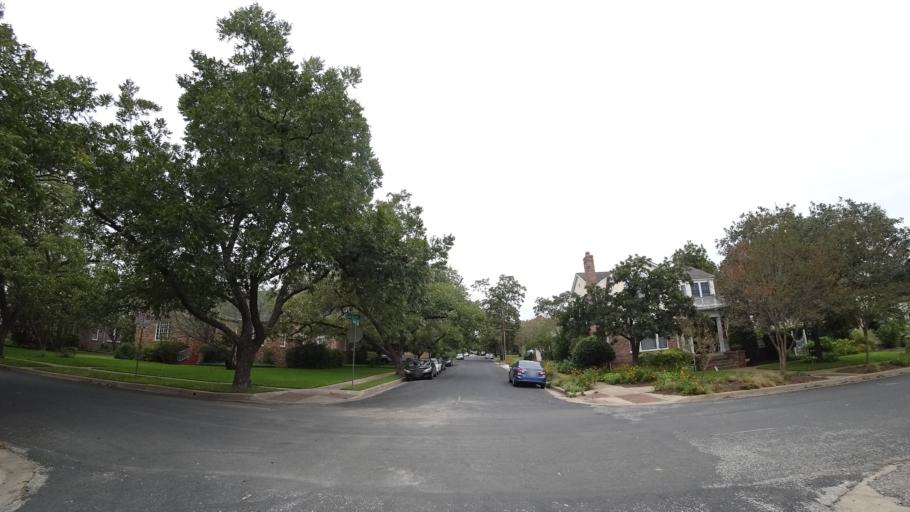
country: US
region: Texas
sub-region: Travis County
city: Austin
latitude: 30.2965
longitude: -97.7301
